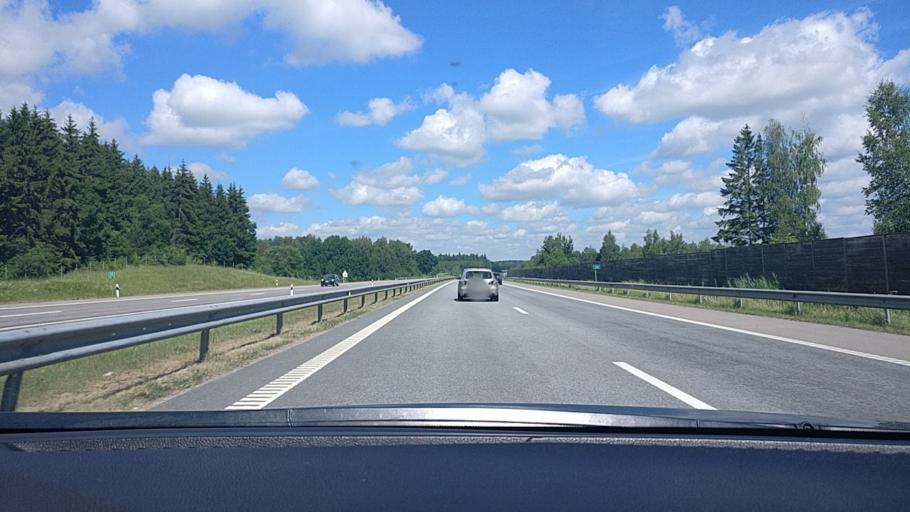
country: LT
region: Vilnius County
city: Pasilaiciai
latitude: 54.8308
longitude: 25.1244
